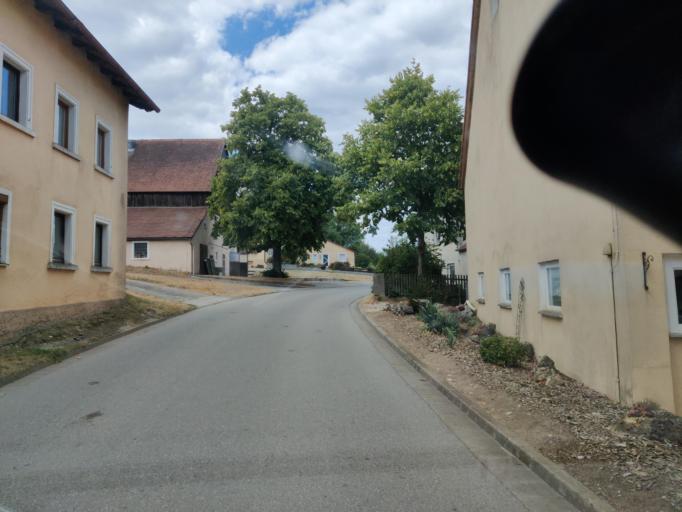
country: DE
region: Bavaria
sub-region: Regierungsbezirk Mittelfranken
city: Thalmassing
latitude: 49.0768
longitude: 11.1895
